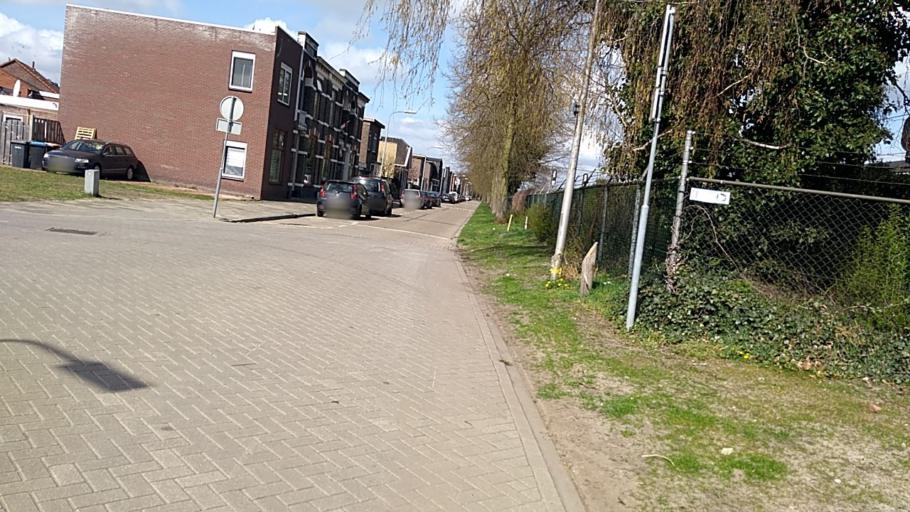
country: NL
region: Overijssel
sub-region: Gemeente Almelo
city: Almelo
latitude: 52.3573
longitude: 6.6545
